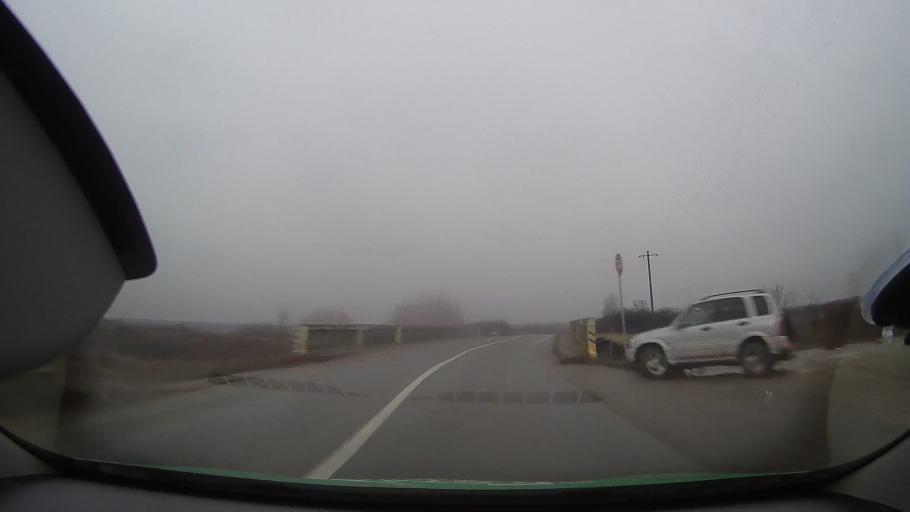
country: RO
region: Bihor
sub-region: Comuna Madaras
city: Madaras
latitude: 46.7960
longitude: 21.7240
